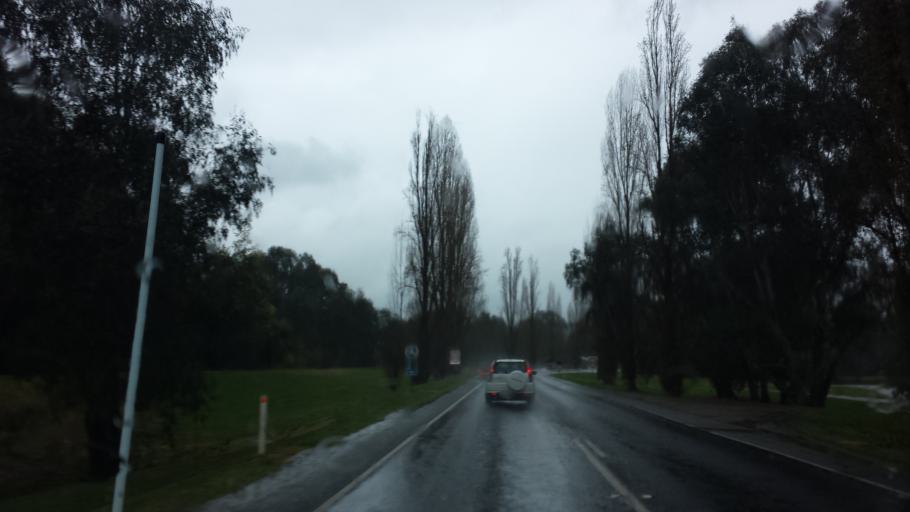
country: AU
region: Victoria
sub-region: Wangaratta
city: Wangaratta
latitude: -36.5523
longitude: 146.7059
